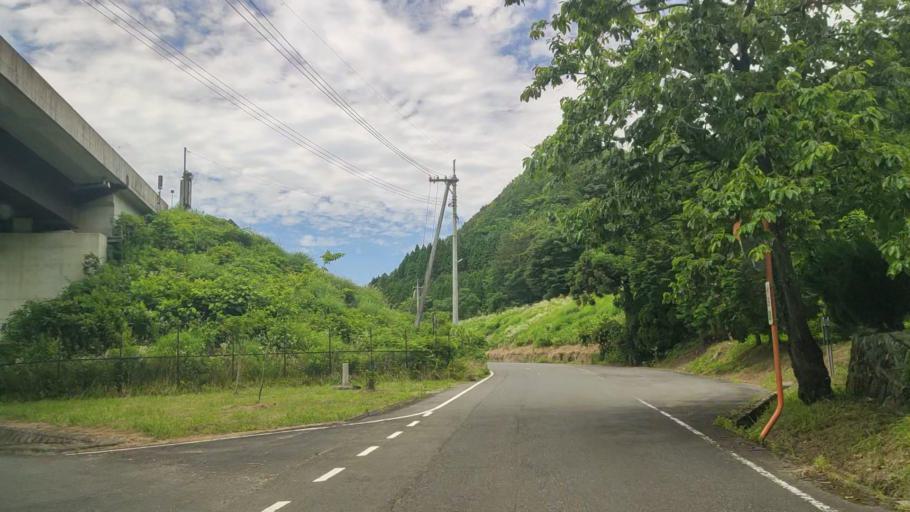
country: JP
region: Hyogo
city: Yamazakicho-nakabirose
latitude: 35.1043
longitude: 134.3296
